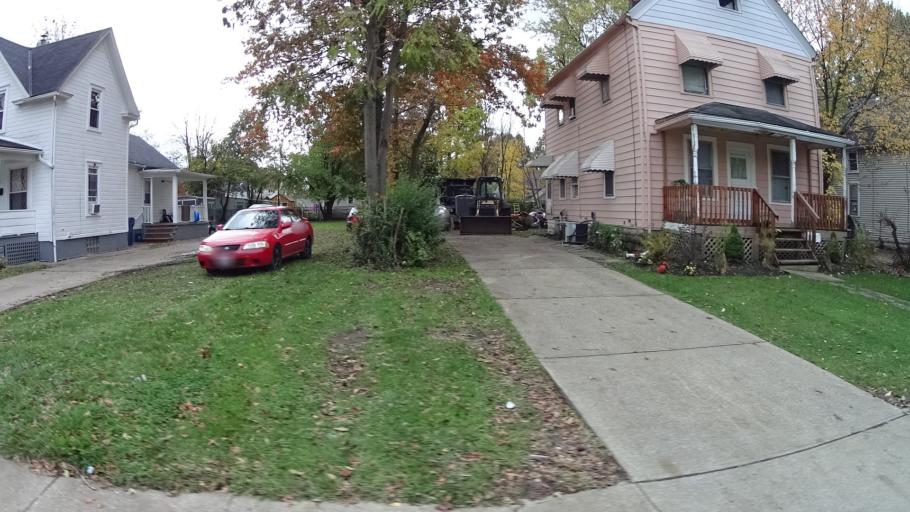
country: US
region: Ohio
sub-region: Lorain County
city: Lorain
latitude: 41.4489
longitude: -82.1714
